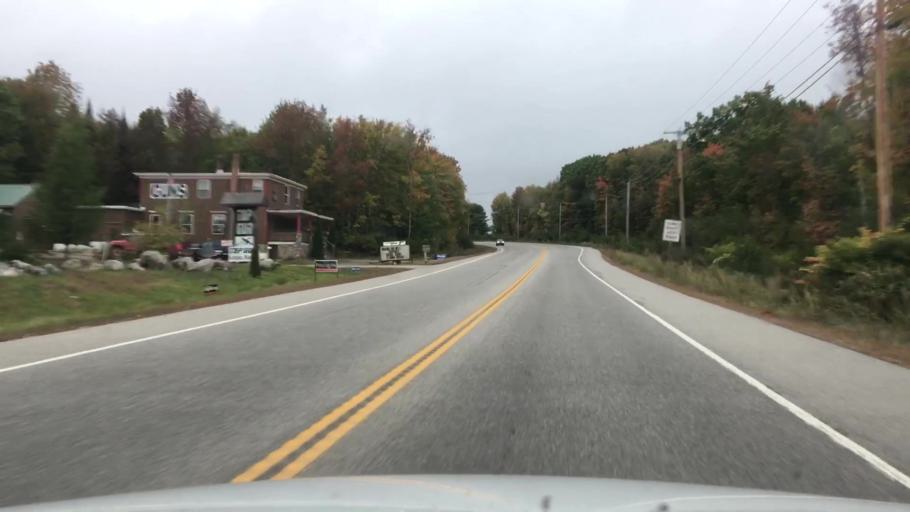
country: US
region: Maine
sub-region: Androscoggin County
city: Poland
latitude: 44.0201
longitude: -70.3637
